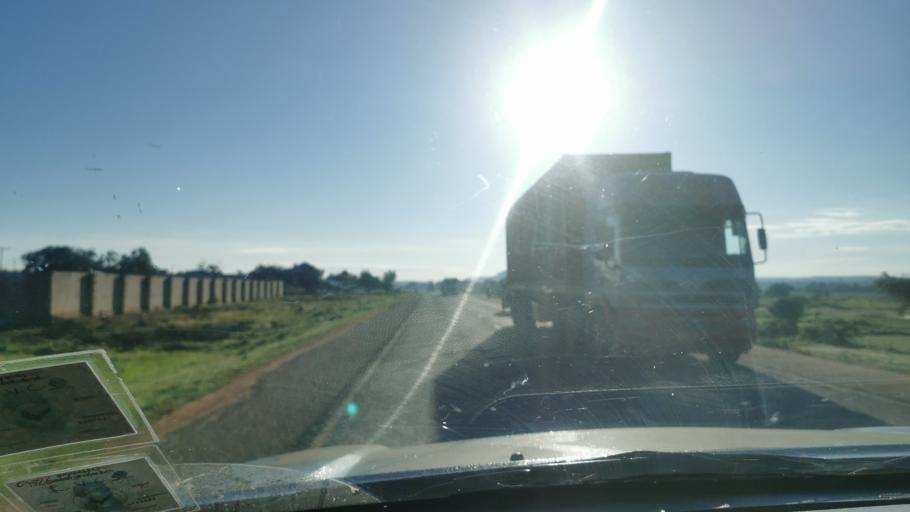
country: TZ
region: Shinyanga
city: Kahama
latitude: -3.8380
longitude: 32.6358
